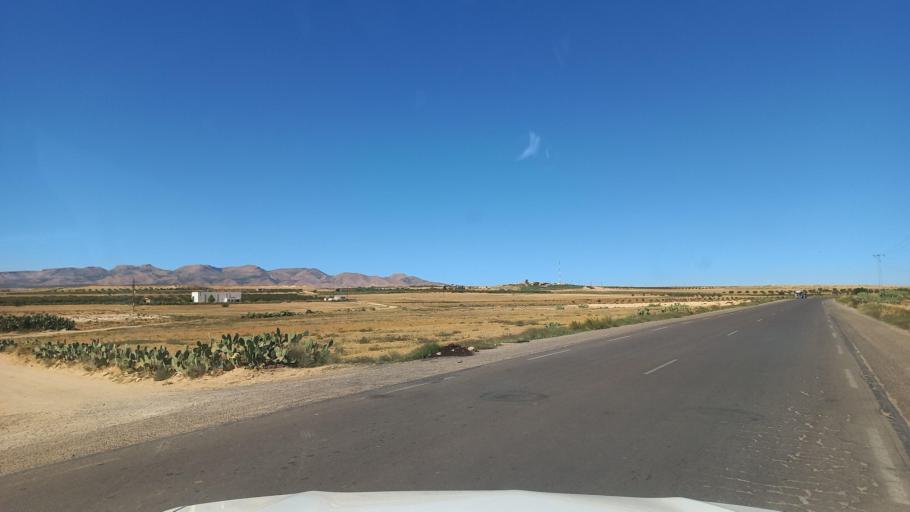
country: TN
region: Al Qasrayn
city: Sbiba
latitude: 35.3673
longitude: 9.0963
